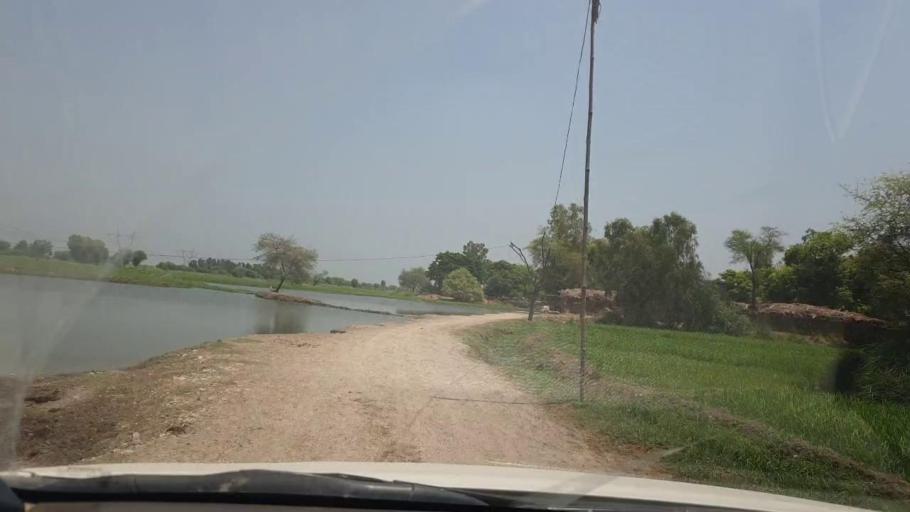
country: PK
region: Sindh
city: Shikarpur
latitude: 27.9189
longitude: 68.6927
